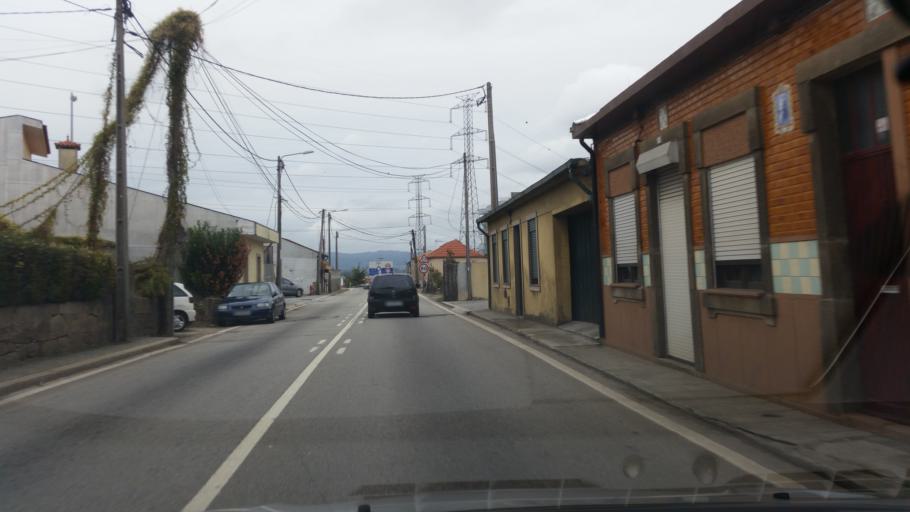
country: PT
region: Porto
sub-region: Valongo
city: Ermesinde
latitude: 41.2329
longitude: -8.5432
